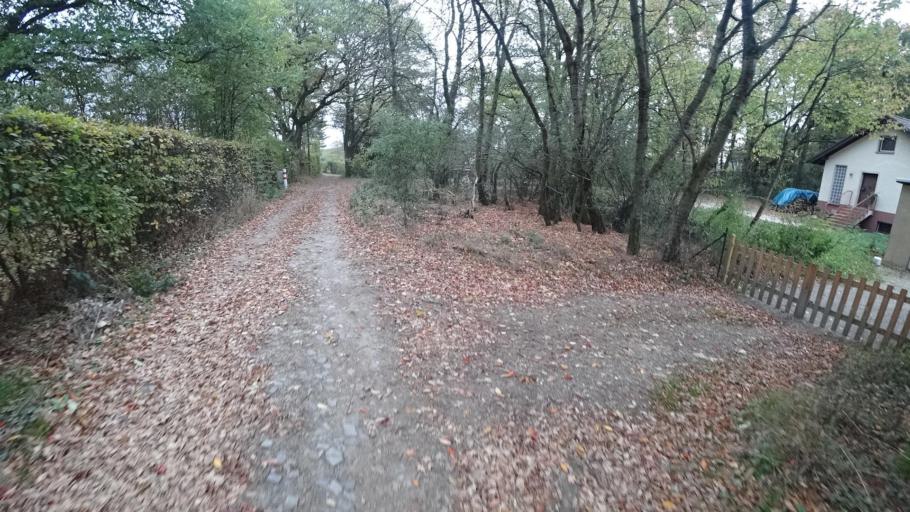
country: DE
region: Rheinland-Pfalz
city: Berg
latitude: 50.5465
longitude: 6.9266
